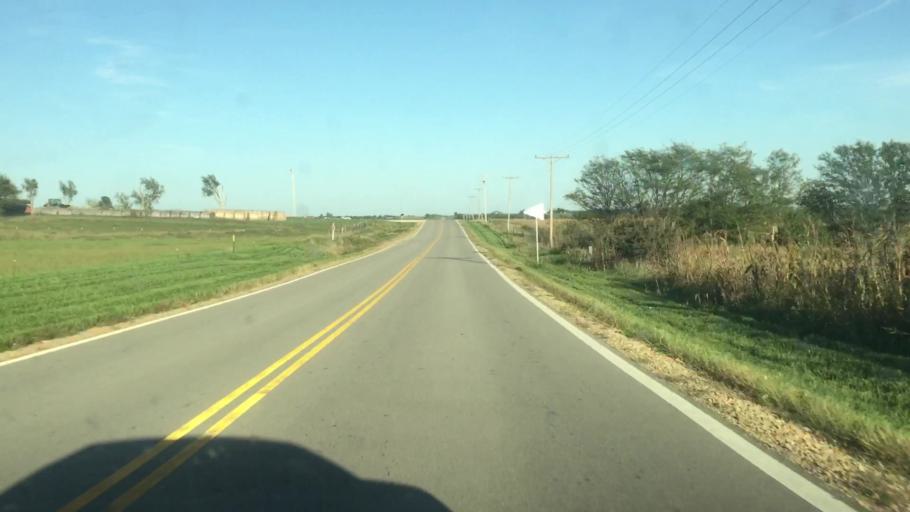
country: US
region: Kansas
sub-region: Brown County
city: Horton
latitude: 39.5876
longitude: -95.5747
